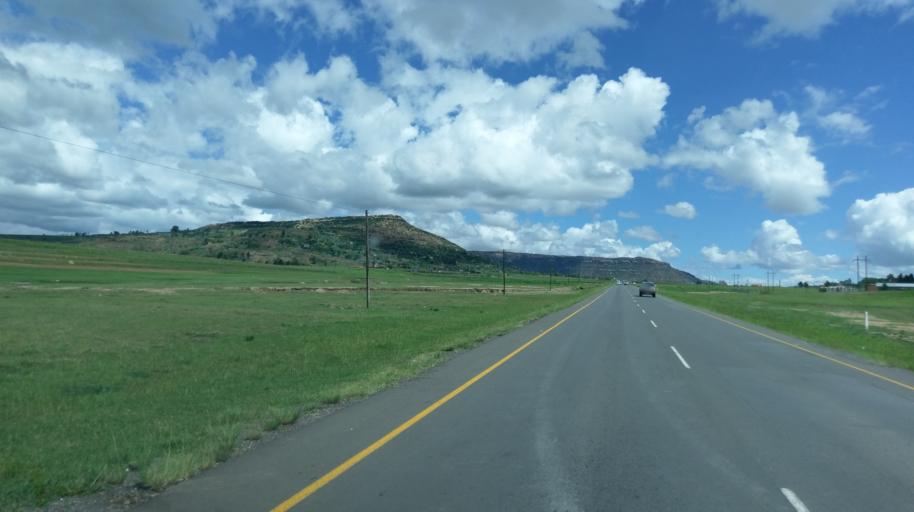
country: LS
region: Maseru
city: Maseru
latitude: -29.5796
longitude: 27.4948
